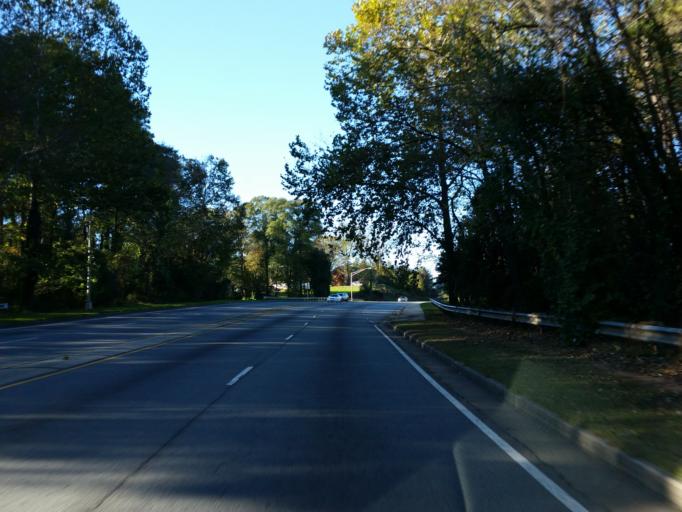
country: US
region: Georgia
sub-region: Cobb County
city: Marietta
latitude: 33.9448
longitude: -84.5444
